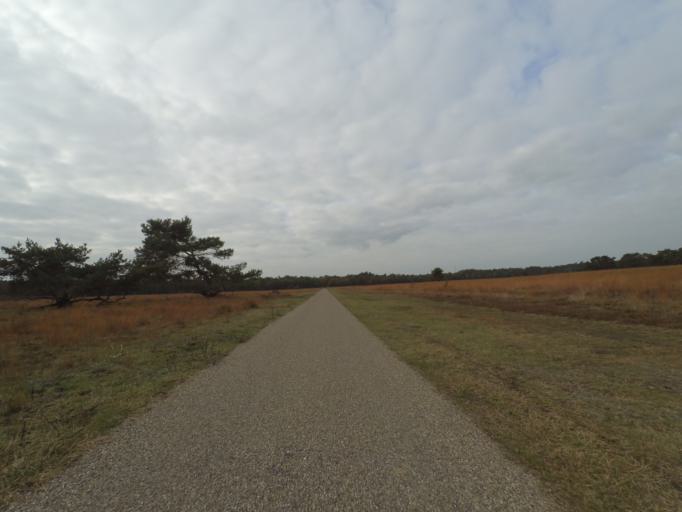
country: NL
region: Gelderland
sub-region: Gemeente Ermelo
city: Ermelo
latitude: 52.3128
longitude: 5.6826
